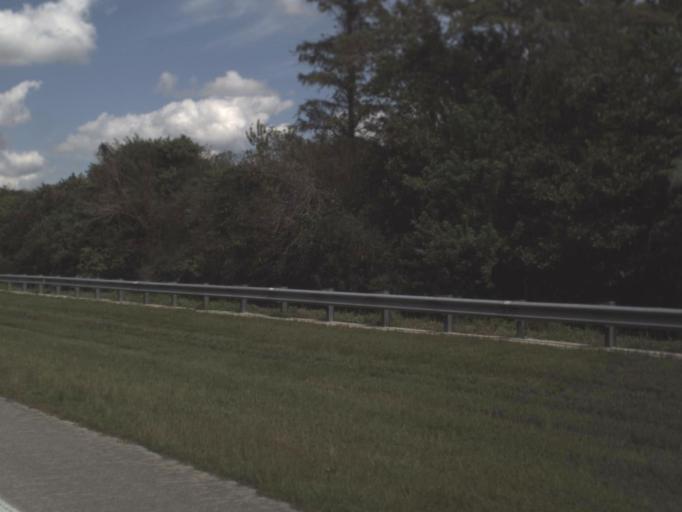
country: US
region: Florida
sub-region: Collier County
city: Orangetree
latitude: 26.0930
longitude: -81.3447
